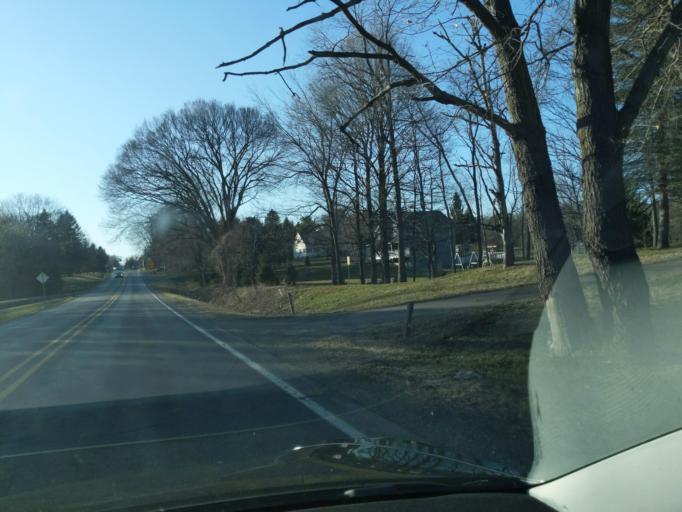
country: US
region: Michigan
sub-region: Washtenaw County
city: Chelsea
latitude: 42.3016
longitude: -84.0017
